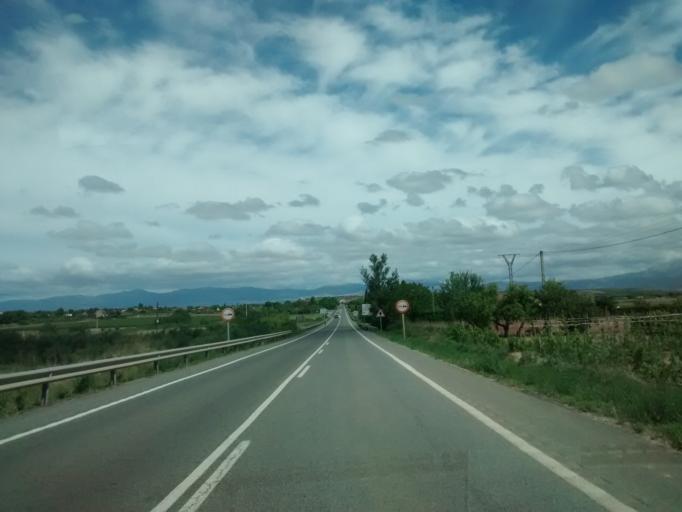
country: ES
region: La Rioja
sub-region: Provincia de La Rioja
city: Villamediana de Iregua
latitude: 42.3987
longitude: -2.4027
